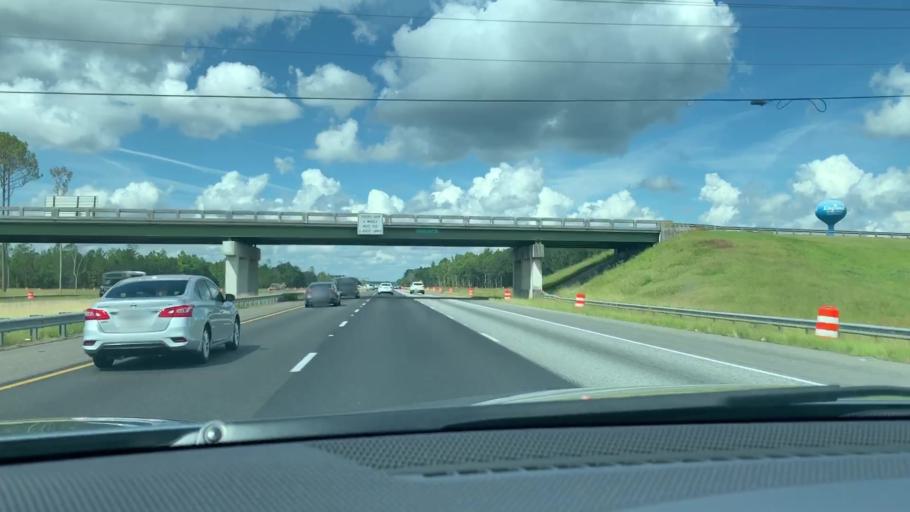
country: US
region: Georgia
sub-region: Camden County
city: Kingsland
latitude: 30.8461
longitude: -81.6718
